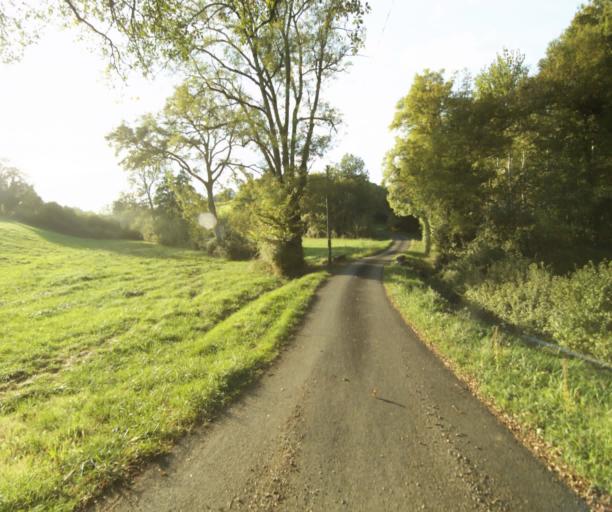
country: FR
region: Midi-Pyrenees
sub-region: Departement du Gers
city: Gondrin
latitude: 43.8789
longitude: 0.2754
